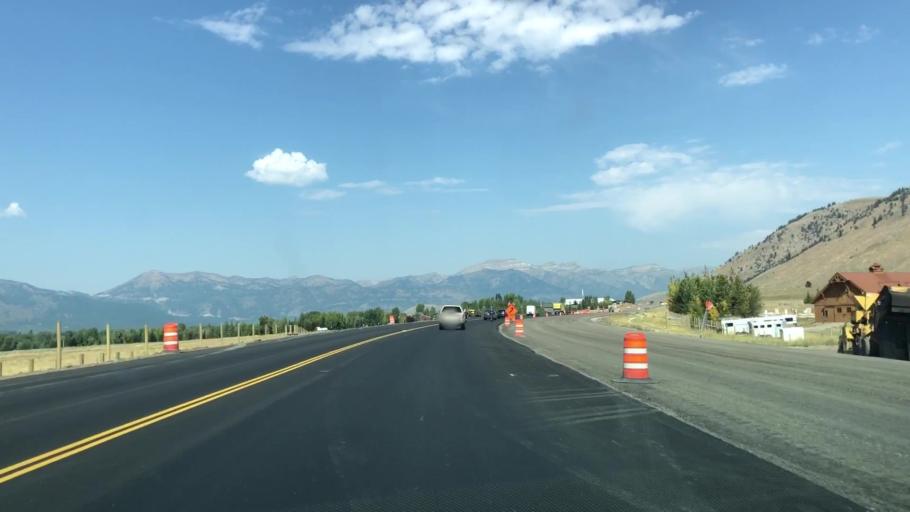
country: US
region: Wyoming
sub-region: Teton County
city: South Park
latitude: 43.4116
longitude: -110.7712
